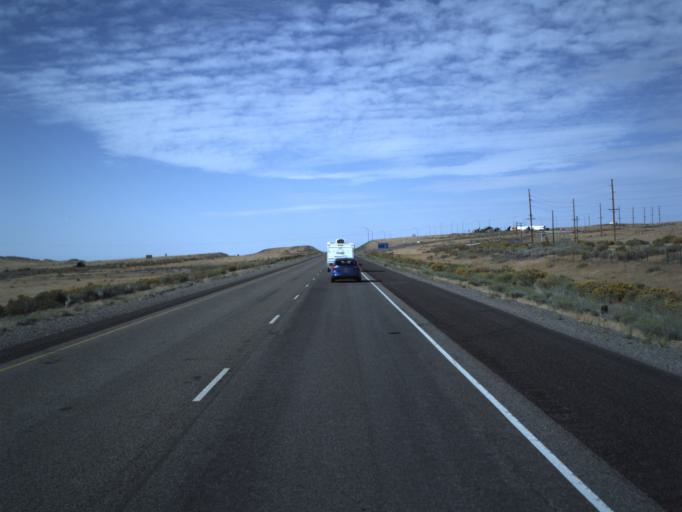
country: US
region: Utah
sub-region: Tooele County
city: Grantsville
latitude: 40.7637
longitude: -113.0000
